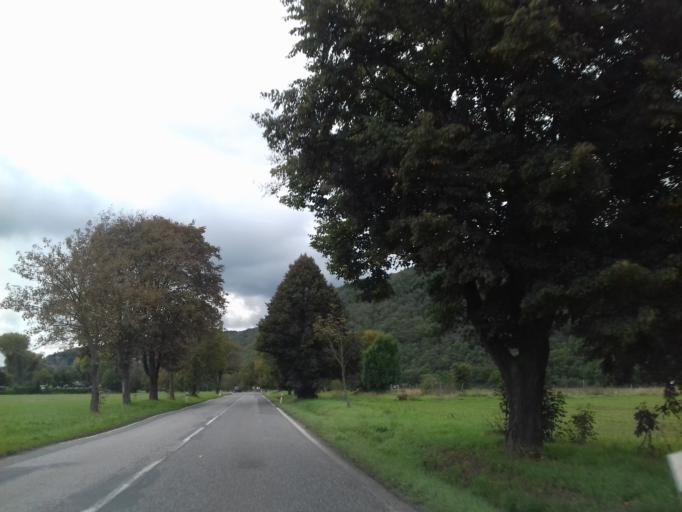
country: CZ
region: Central Bohemia
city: Cernosice
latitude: 49.9701
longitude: 14.3387
